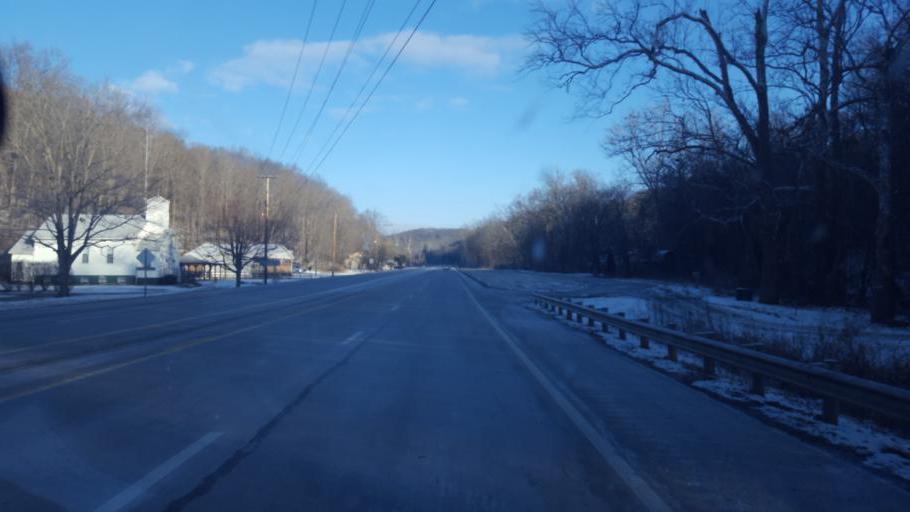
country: US
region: Ohio
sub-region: Pike County
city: Waverly
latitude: 39.1886
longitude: -82.9787
